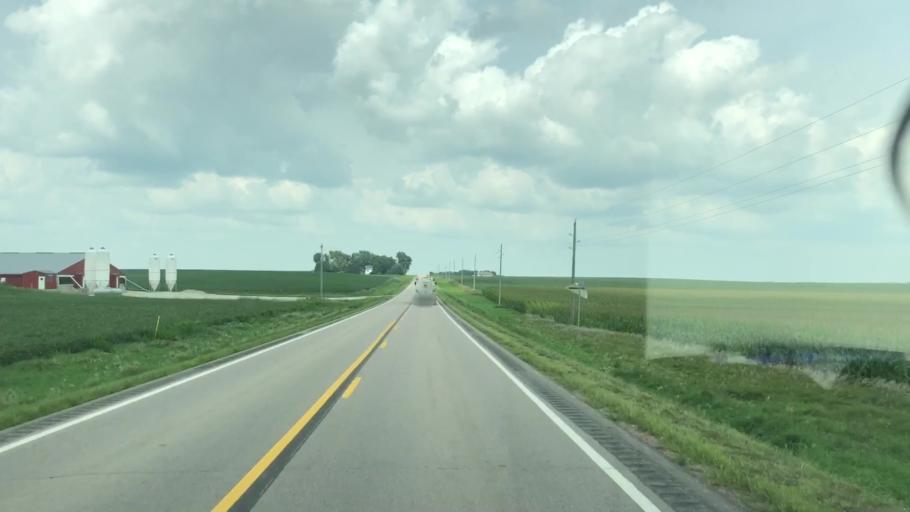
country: US
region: Iowa
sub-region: Plymouth County
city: Remsen
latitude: 42.7843
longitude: -95.9579
